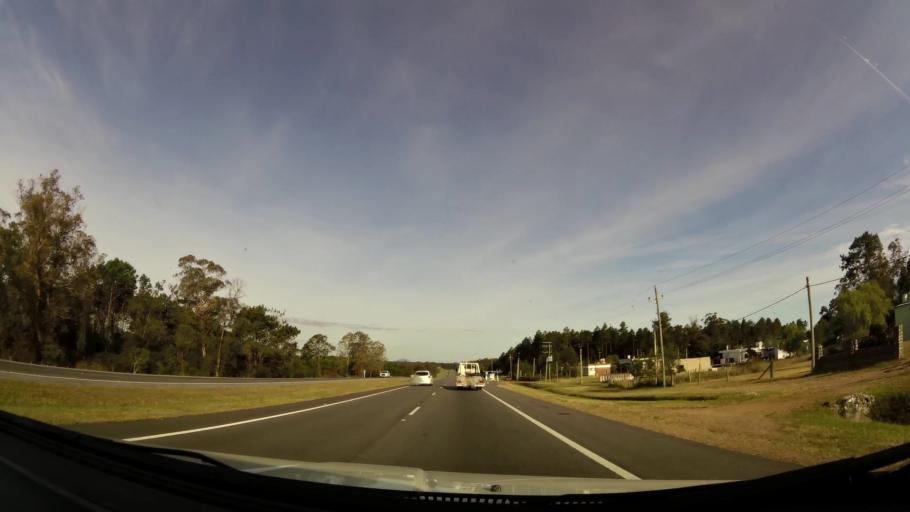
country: UY
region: Canelones
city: La Floresta
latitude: -34.7850
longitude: -55.5319
